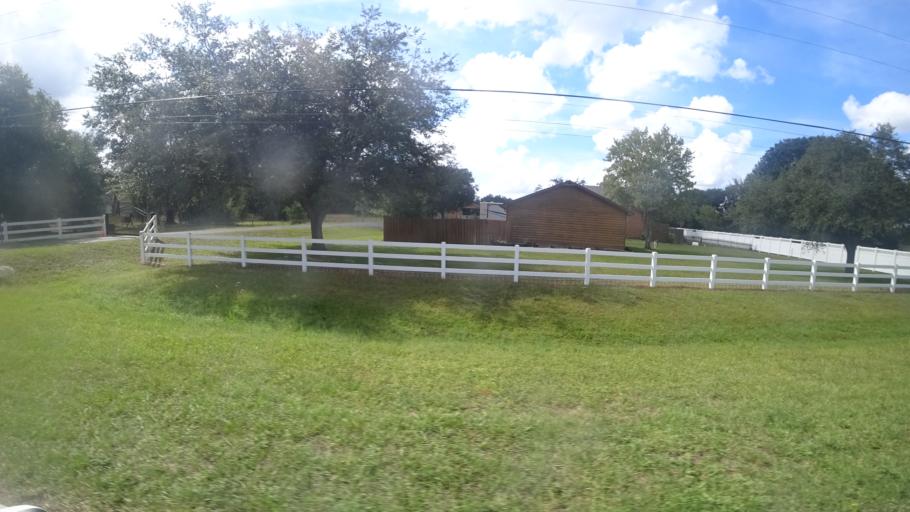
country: US
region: Florida
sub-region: Hillsborough County
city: Sun City Center
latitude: 27.6537
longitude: -82.3850
